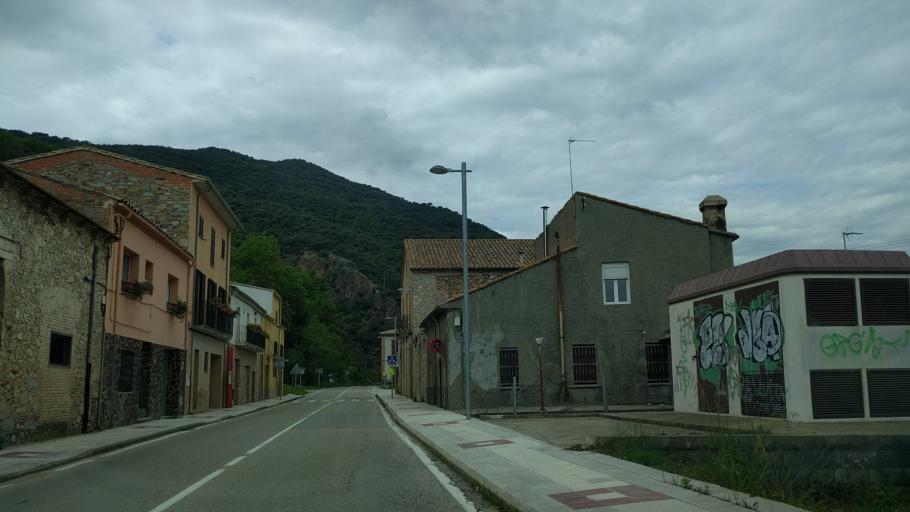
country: ES
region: Catalonia
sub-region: Provincia de Girona
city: la Cellera de Ter
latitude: 41.9835
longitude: 2.6066
